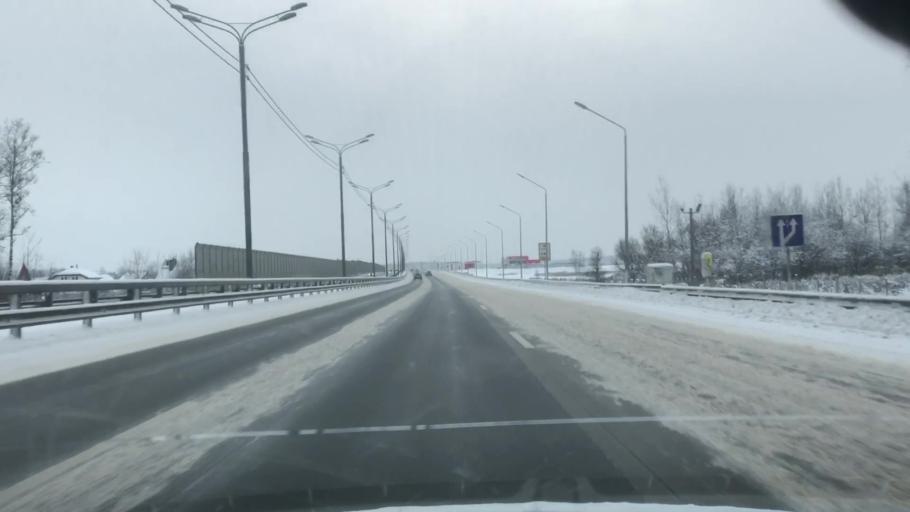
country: RU
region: Moskovskaya
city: Barybino
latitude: 55.1972
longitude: 37.8902
